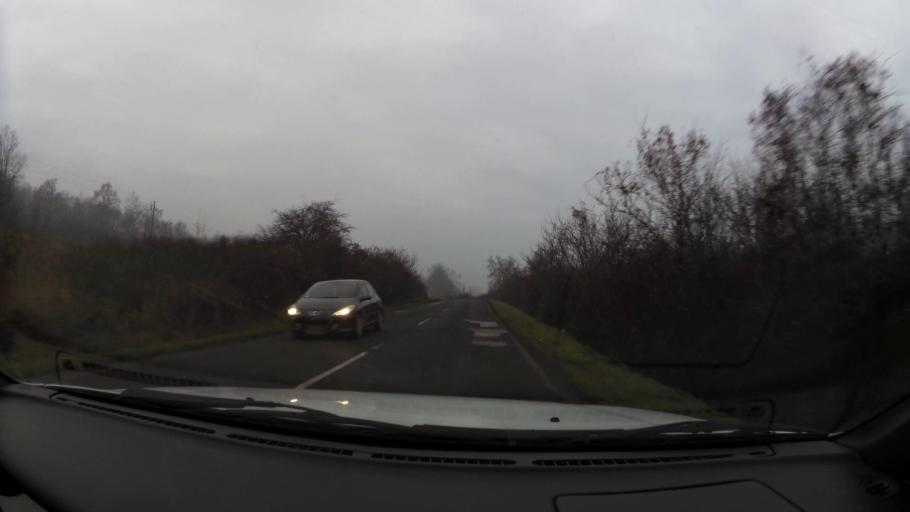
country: HU
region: Borsod-Abauj-Zemplen
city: Rudabanya
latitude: 48.3525
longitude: 20.6370
